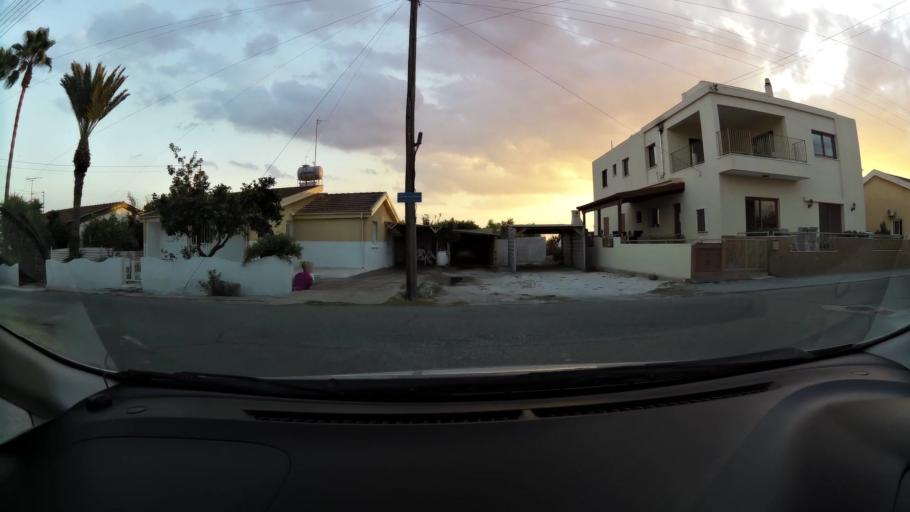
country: CY
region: Larnaka
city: Dhromolaxia
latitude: 34.8712
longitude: 33.5836
